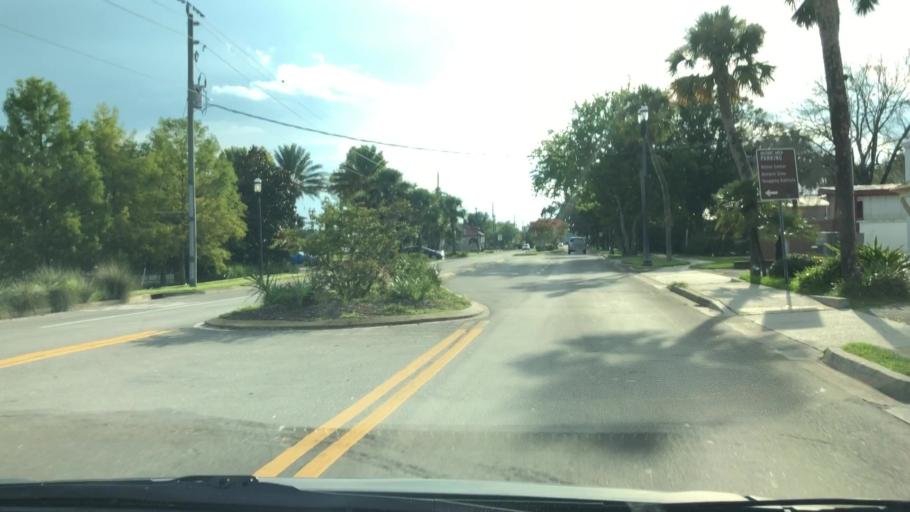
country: US
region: Florida
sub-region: Saint Johns County
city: Saint Augustine
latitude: 29.8994
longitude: -81.3159
